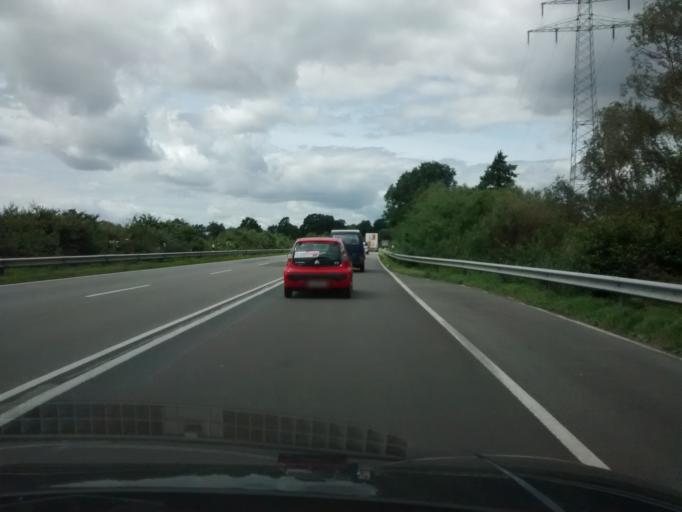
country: DE
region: Lower Saxony
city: Emstek
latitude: 52.8175
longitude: 8.1405
